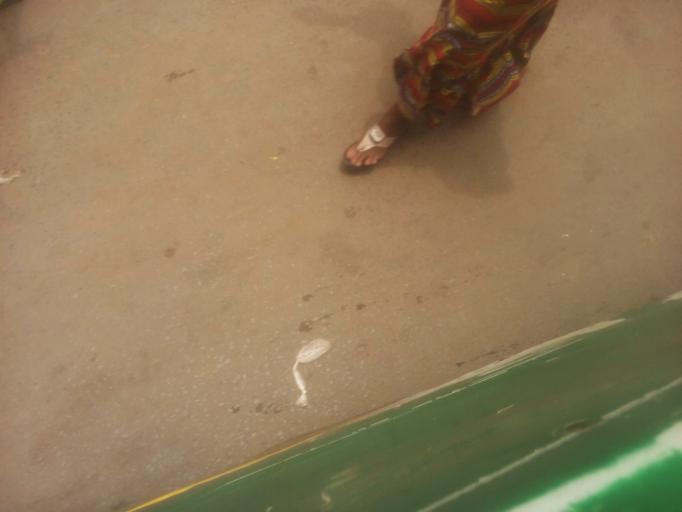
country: ML
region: Bamako
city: Bamako
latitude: 12.6490
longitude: -7.9931
